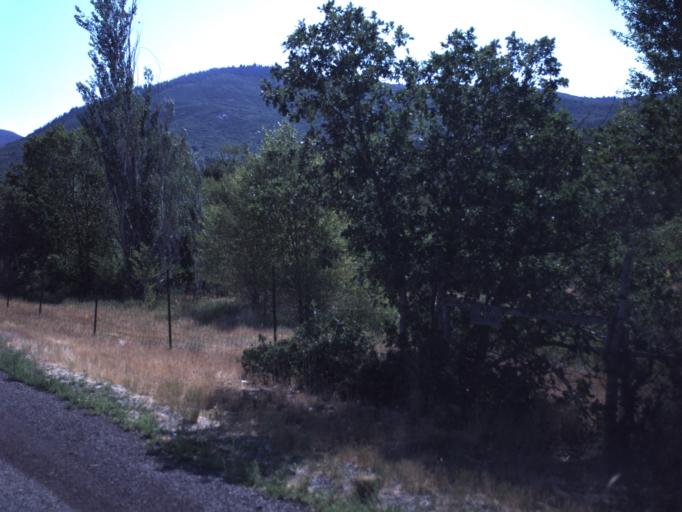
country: US
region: Utah
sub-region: Sanpete County
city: Fairview
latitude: 39.6412
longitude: -111.4201
